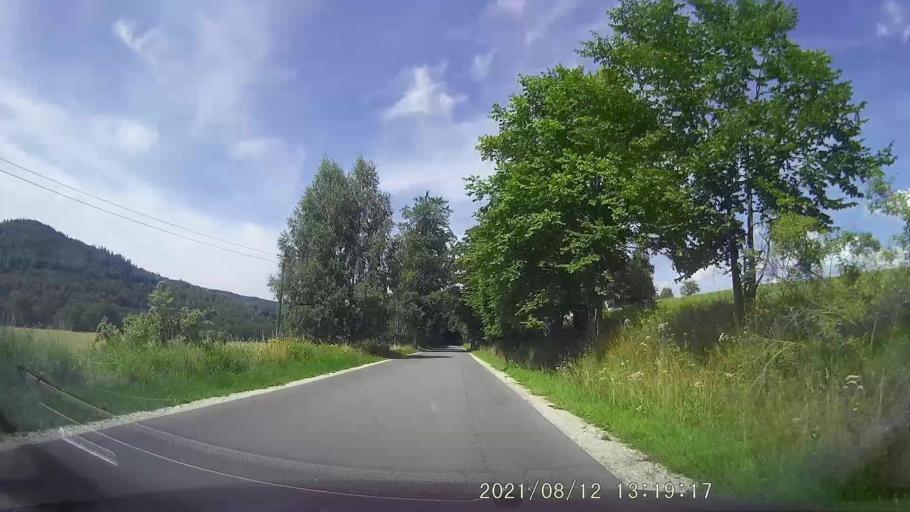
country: PL
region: Lower Silesian Voivodeship
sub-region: Powiat klodzki
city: Stronie Slaskie
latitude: 50.2777
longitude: 16.8840
